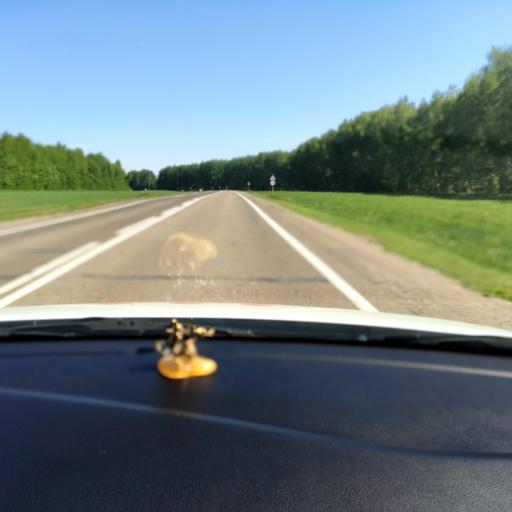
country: RU
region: Tatarstan
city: Vysokaya Gora
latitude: 56.0945
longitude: 49.1812
